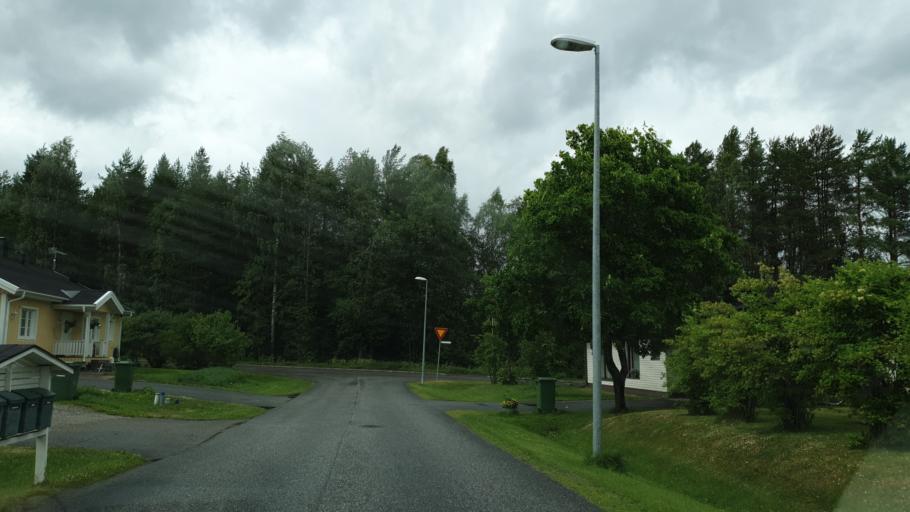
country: FI
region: Kainuu
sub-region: Kehys-Kainuu
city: Kuhmo
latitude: 64.1198
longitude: 29.5065
